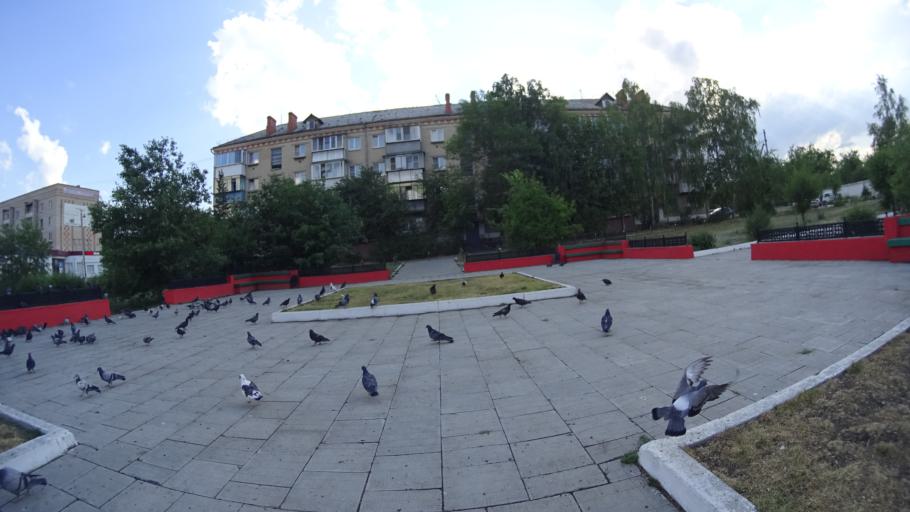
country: RU
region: Chelyabinsk
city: Troitsk
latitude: 54.0837
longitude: 61.5412
